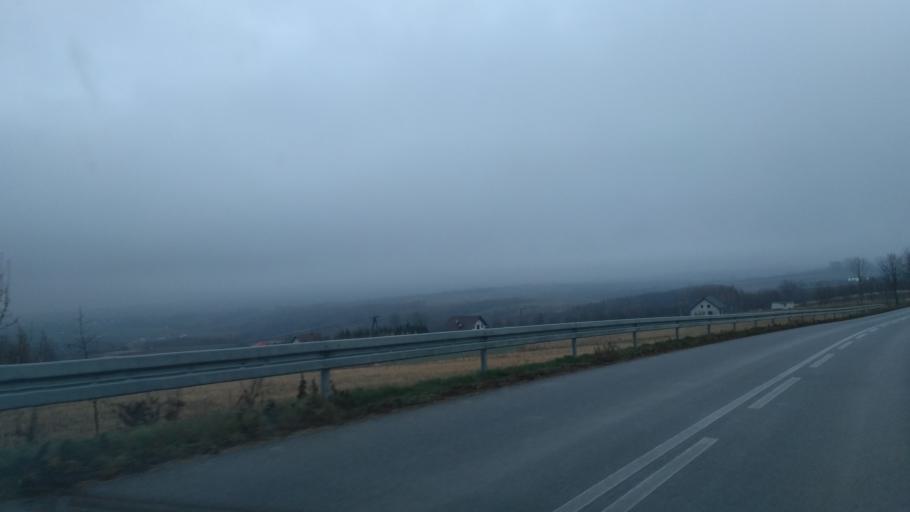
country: PL
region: Subcarpathian Voivodeship
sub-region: Powiat jaroslawski
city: Jodlowka
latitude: 49.9042
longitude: 22.4898
